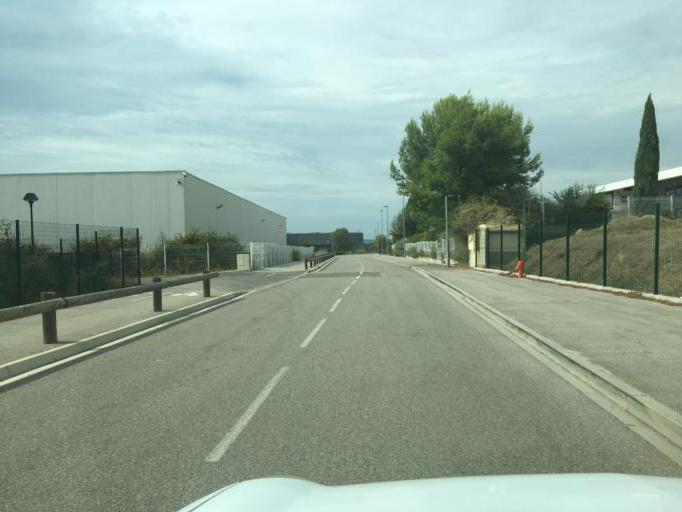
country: FR
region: Provence-Alpes-Cote d'Azur
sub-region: Departement des Bouches-du-Rhone
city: Bouc-Bel-Air
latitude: 43.4834
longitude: 5.3896
